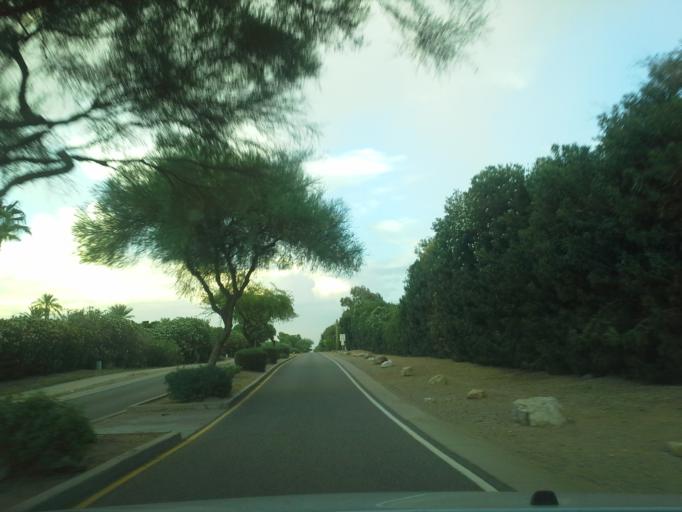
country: US
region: Arizona
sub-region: Maricopa County
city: Paradise Valley
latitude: 33.5238
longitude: -111.9601
